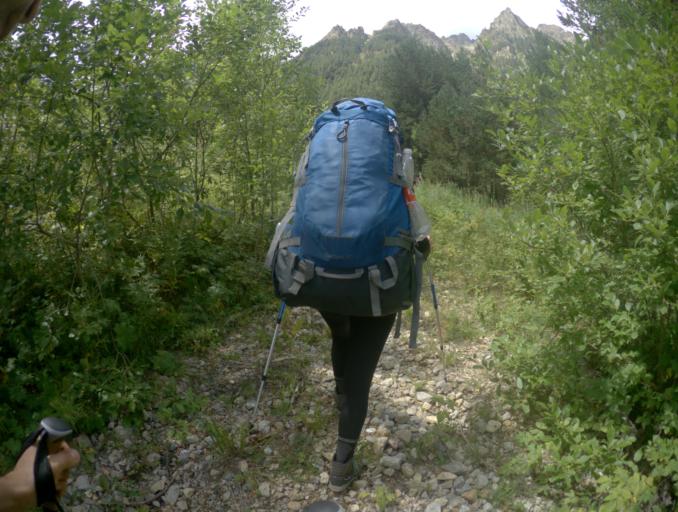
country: RU
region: Karachayevo-Cherkesiya
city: Uchkulan
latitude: 43.3497
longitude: 42.1571
